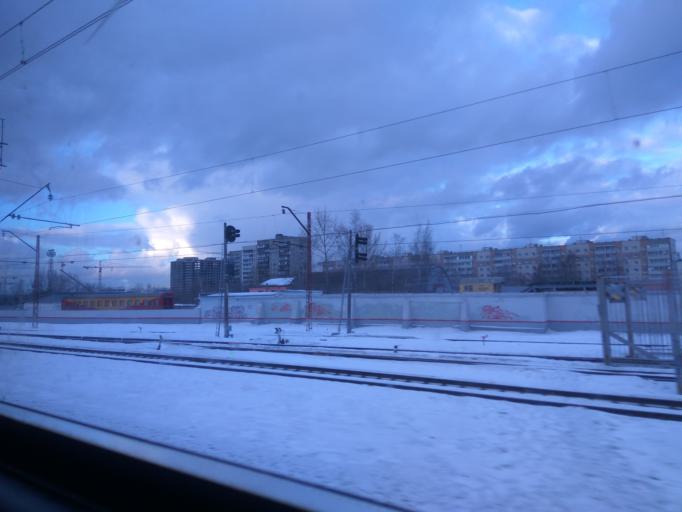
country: RU
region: Moskovskaya
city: Biryulevo Zapadnoye
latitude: 55.5979
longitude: 37.6511
